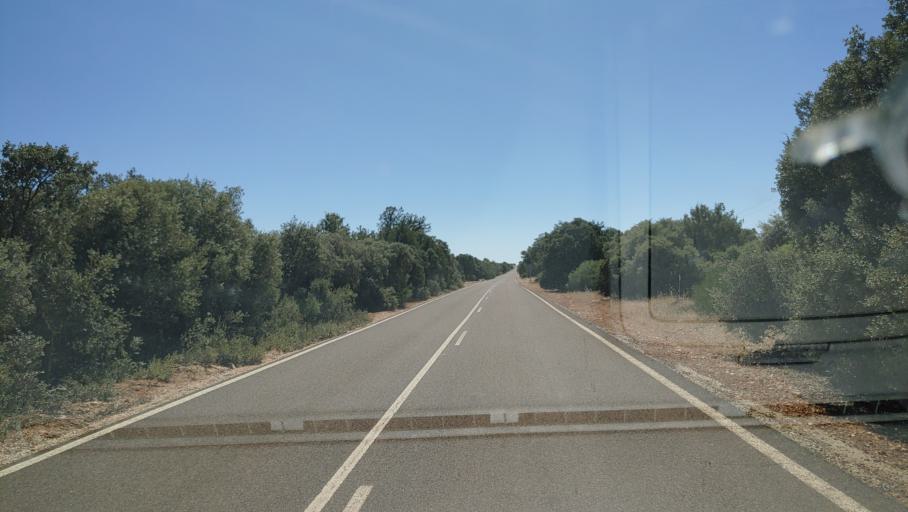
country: ES
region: Castille-La Mancha
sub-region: Provincia de Ciudad Real
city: Villahermosa
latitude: 38.8232
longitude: -2.8295
